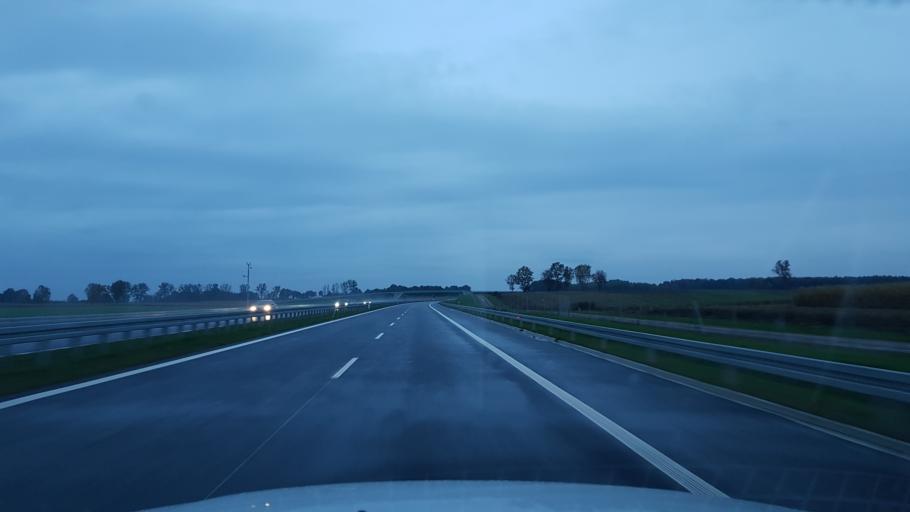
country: PL
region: West Pomeranian Voivodeship
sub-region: Powiat gryficki
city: Brojce
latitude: 53.9030
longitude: 15.3820
